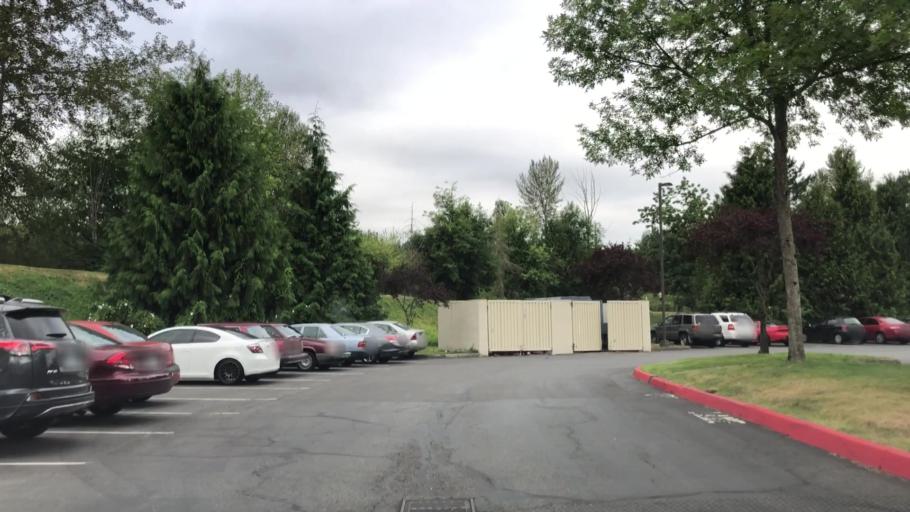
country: US
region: Washington
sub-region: King County
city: Bothell
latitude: 47.7735
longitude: -122.1829
